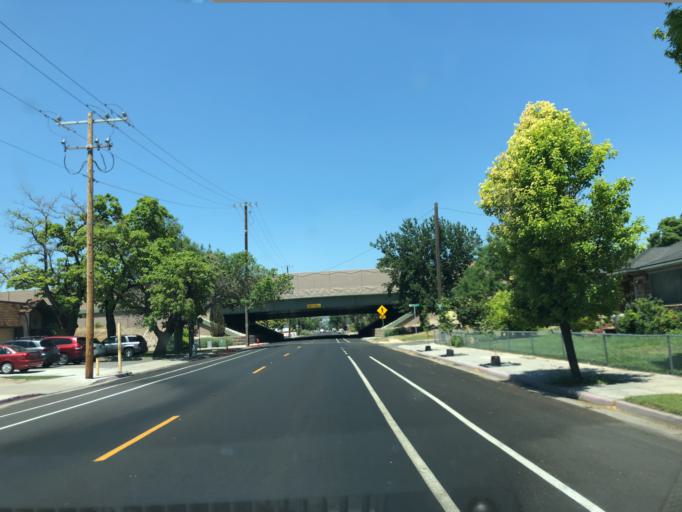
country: US
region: Utah
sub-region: Salt Lake County
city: South Salt Lake
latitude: 40.7172
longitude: -111.8826
